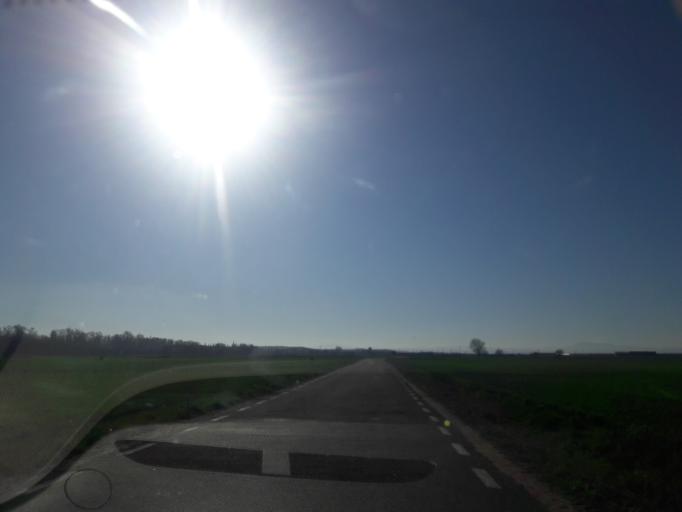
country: ES
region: Castille and Leon
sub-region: Provincia de Salamanca
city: Coca de Alba
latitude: 40.8636
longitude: -5.3695
